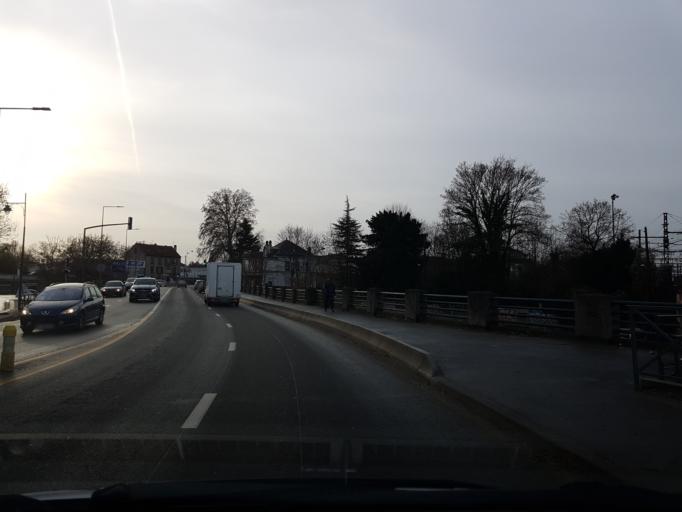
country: FR
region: Ile-de-France
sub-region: Departement du Val-de-Marne
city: Villeneuve-Saint-Georges
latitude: 48.7261
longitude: 2.4445
